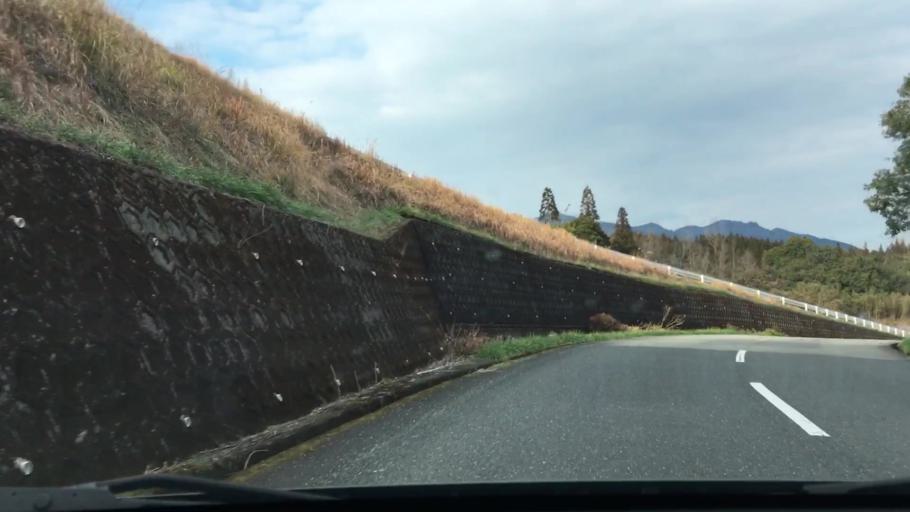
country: JP
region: Miyazaki
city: Nichinan
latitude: 31.6177
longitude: 131.3353
